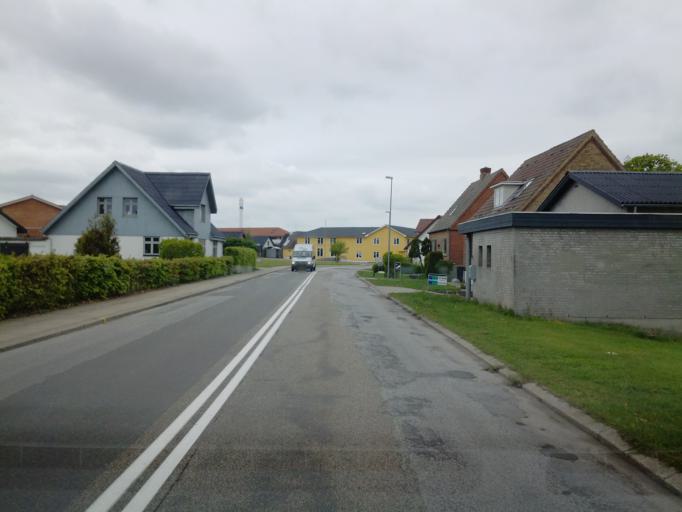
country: DK
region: North Denmark
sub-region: Bronderslev Kommune
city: Hjallerup
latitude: 57.1685
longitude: 10.1531
